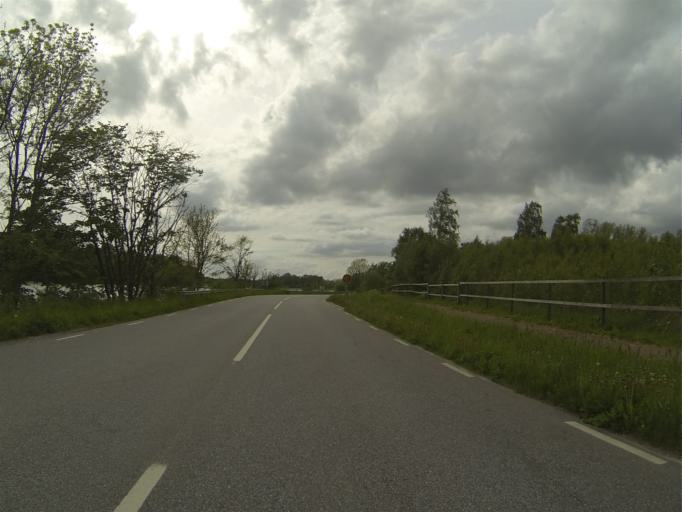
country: SE
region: Skane
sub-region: Lunds Kommun
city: Genarp
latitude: 55.6960
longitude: 13.3281
